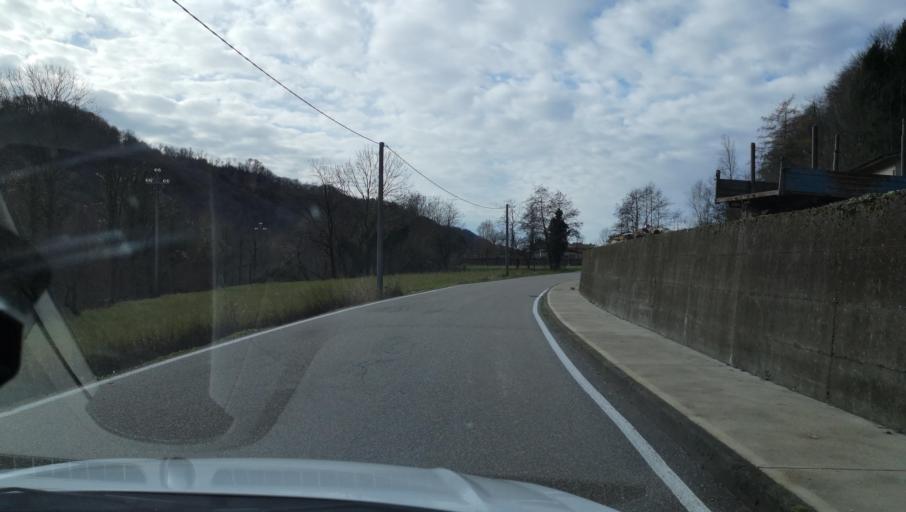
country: IT
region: Friuli Venezia Giulia
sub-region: Provincia di Udine
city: Attimis
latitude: 46.2124
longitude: 13.3078
